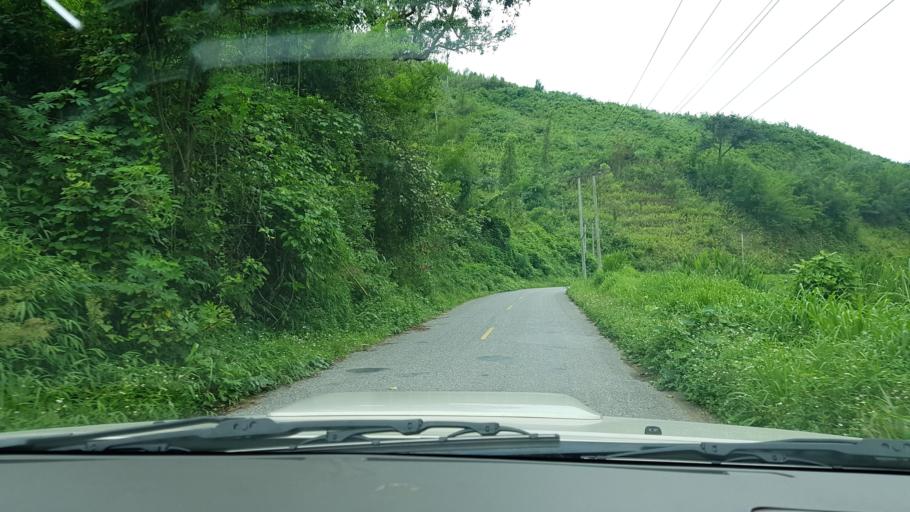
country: LA
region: Oudomxai
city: Muang La
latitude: 20.9346
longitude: 102.2056
